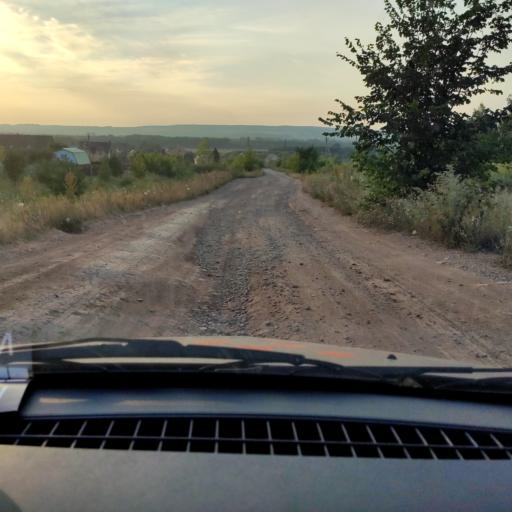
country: RU
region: Bashkortostan
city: Avdon
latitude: 54.5871
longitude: 55.6793
